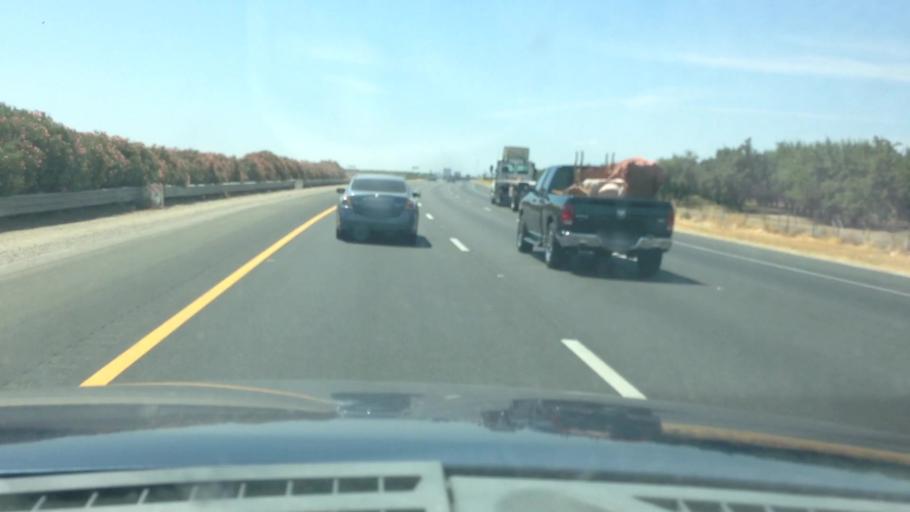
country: US
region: California
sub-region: Kern County
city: McFarland
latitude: 35.6418
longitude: -119.2190
